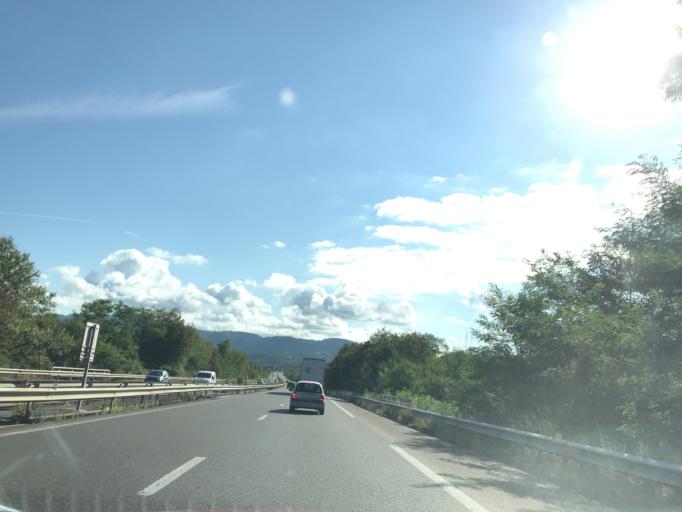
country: FR
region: Auvergne
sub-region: Departement du Puy-de-Dome
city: Peschadoires
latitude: 45.8556
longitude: 3.4804
